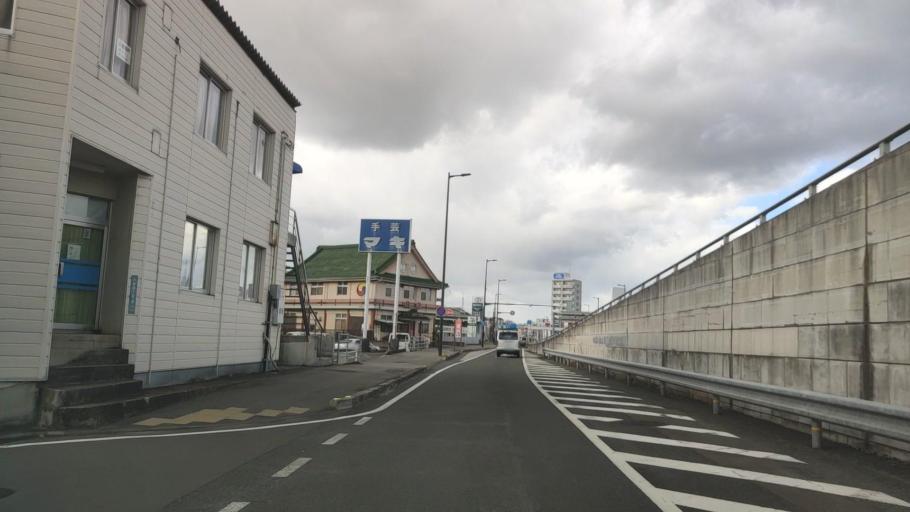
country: JP
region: Ehime
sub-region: Shikoku-chuo Shi
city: Matsuyama
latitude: 33.8277
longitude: 132.7822
